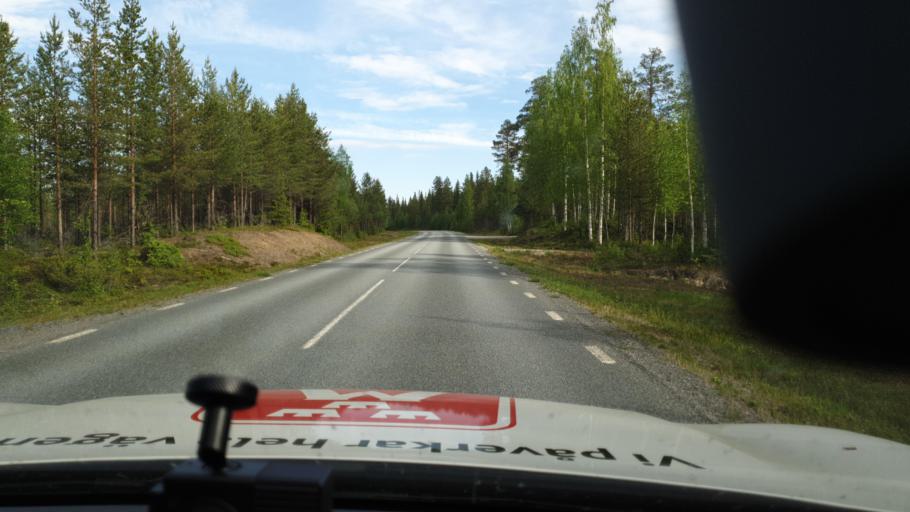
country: SE
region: Vaesterbotten
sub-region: Lycksele Kommun
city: Soderfors
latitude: 65.1338
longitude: 18.2706
